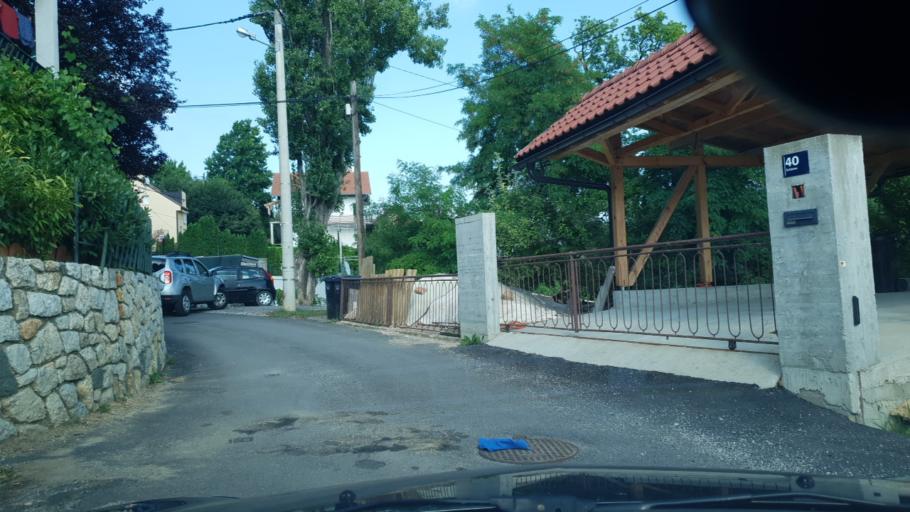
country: HR
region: Grad Zagreb
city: Zagreb
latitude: 45.8584
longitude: 15.9623
